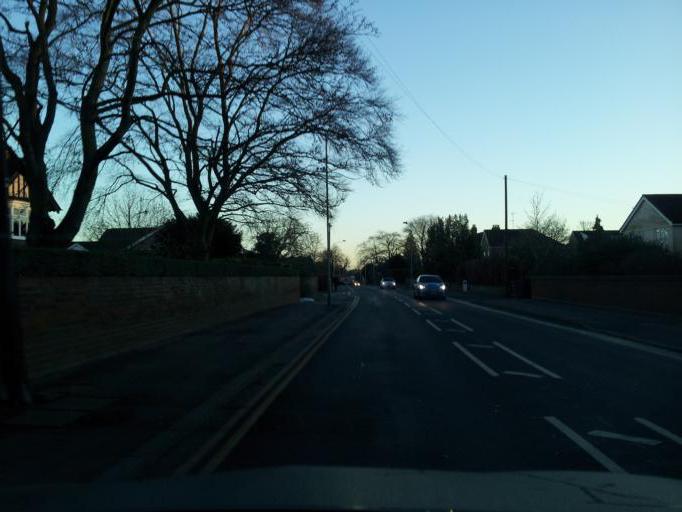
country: GB
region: England
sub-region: Essex
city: Chelmsford
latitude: 51.7411
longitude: 0.4918
